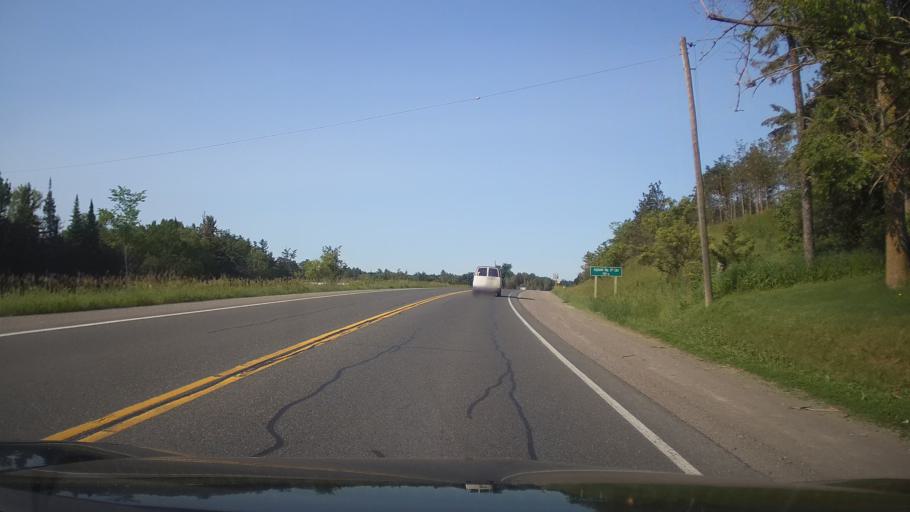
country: CA
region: Ontario
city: Peterborough
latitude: 44.3754
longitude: -77.9868
